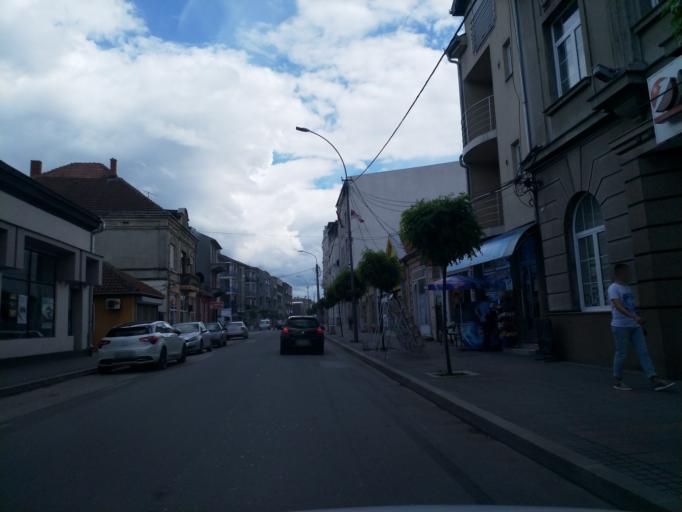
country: RS
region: Central Serbia
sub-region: Pomoravski Okrug
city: Cuprija
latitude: 43.9359
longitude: 21.3702
